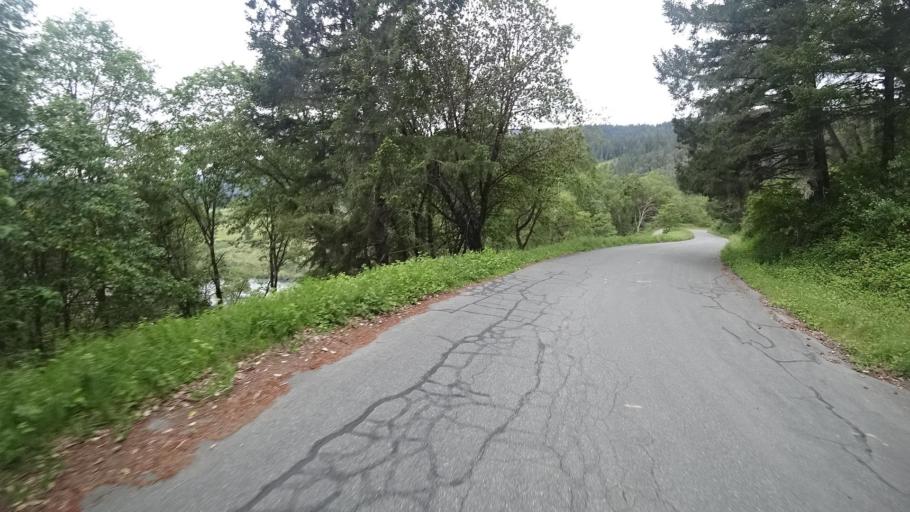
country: US
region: California
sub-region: Humboldt County
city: Willow Creek
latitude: 41.1031
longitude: -123.7078
